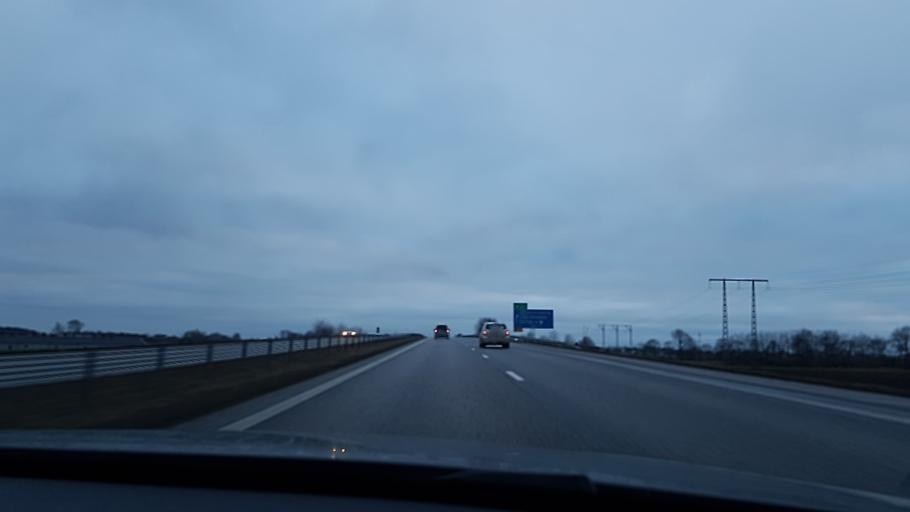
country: SE
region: Skane
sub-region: Astorps Kommun
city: Astorp
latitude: 56.1530
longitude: 12.9471
